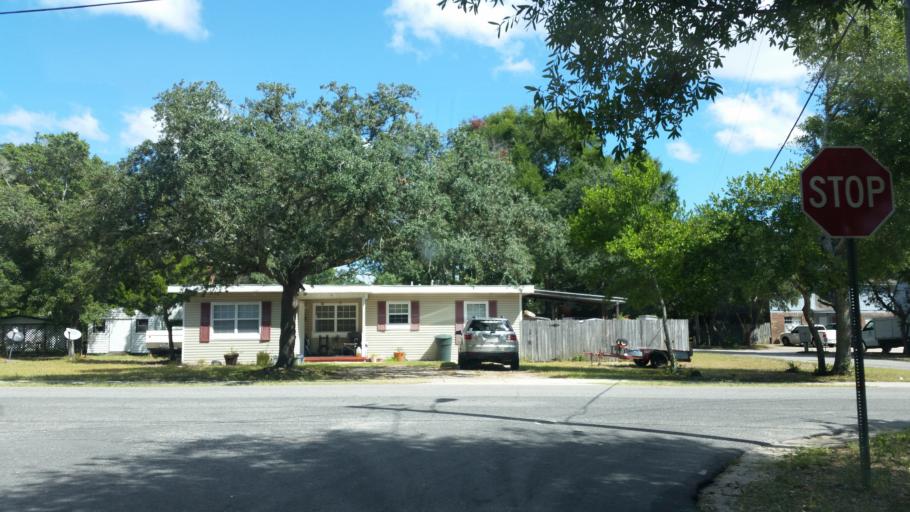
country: US
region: Florida
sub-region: Okaloosa County
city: Fort Walton Beach
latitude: 30.4208
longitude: -86.6150
